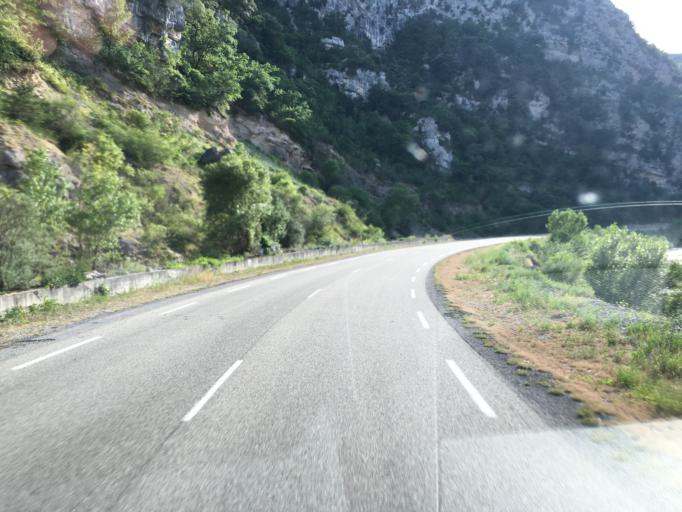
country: FR
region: Rhone-Alpes
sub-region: Departement de la Drome
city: Buis-les-Baronnies
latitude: 44.4312
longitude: 5.3028
